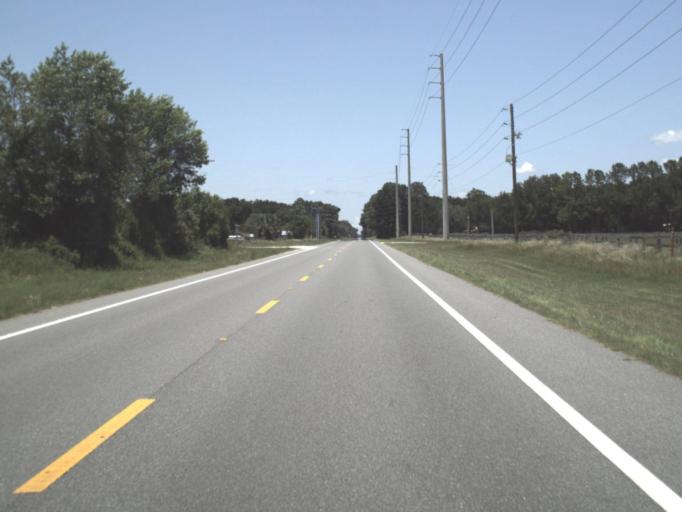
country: US
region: Florida
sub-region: Dixie County
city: Cross City
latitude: 29.6999
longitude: -82.9844
